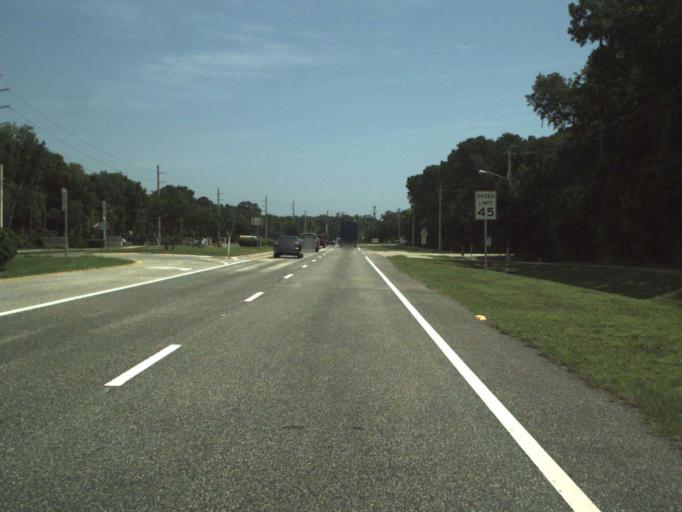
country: US
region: Florida
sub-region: Volusia County
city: Port Orange
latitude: 29.1336
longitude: -81.0002
